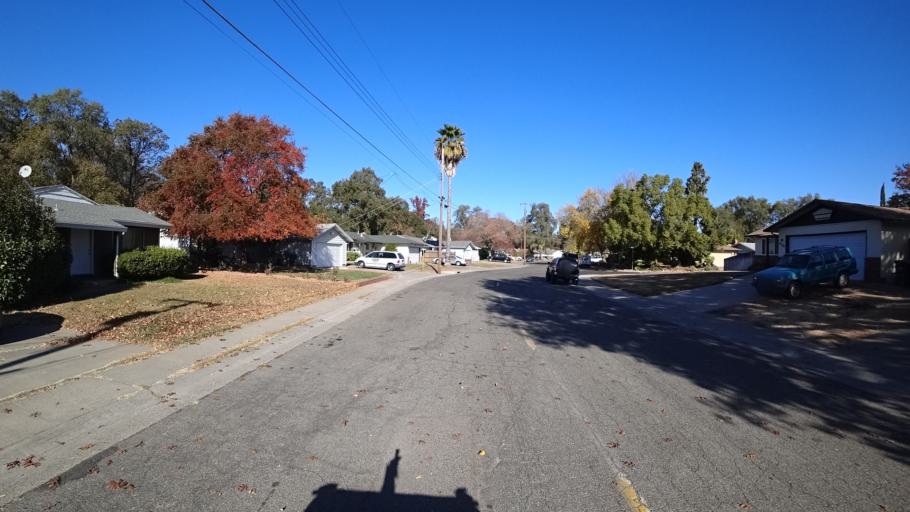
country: US
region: California
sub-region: Sacramento County
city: Antelope
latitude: 38.6854
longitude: -121.3176
